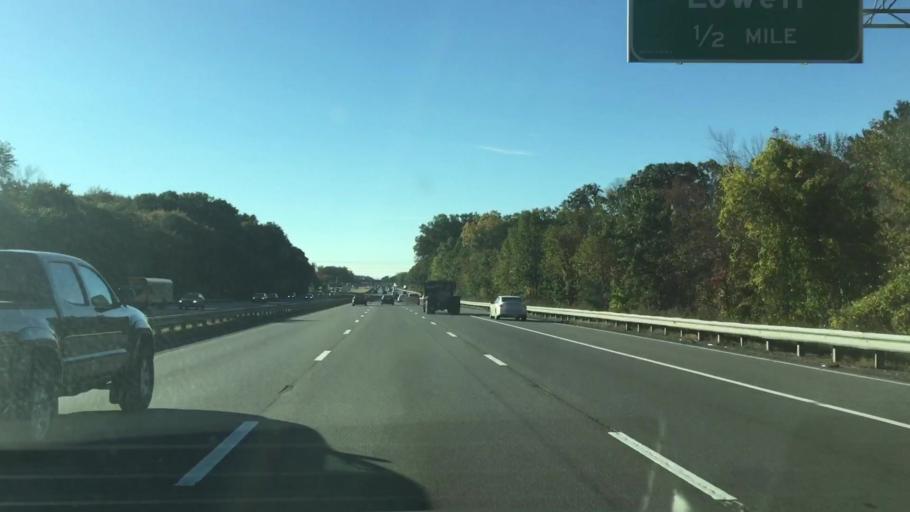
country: US
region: Massachusetts
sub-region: Essex County
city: Lawrence
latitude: 42.6753
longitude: -71.1995
